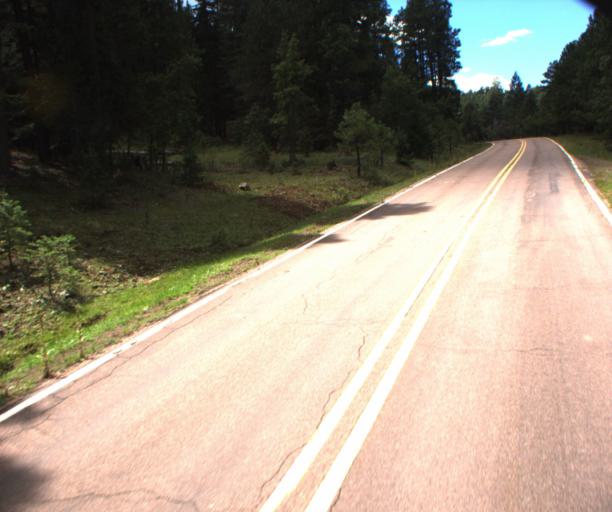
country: US
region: Arizona
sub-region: Navajo County
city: Pinetop-Lakeside
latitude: 34.0296
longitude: -109.7601
